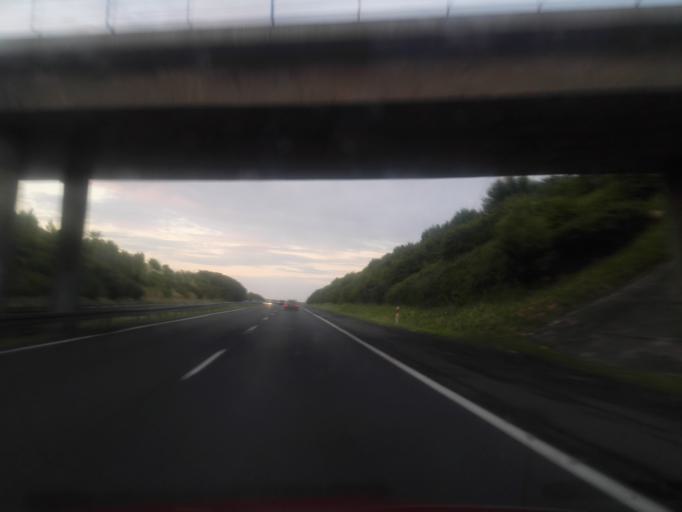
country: PL
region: Lodz Voivodeship
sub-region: Powiat radomszczanski
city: Radomsko
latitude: 51.1391
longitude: 19.4234
